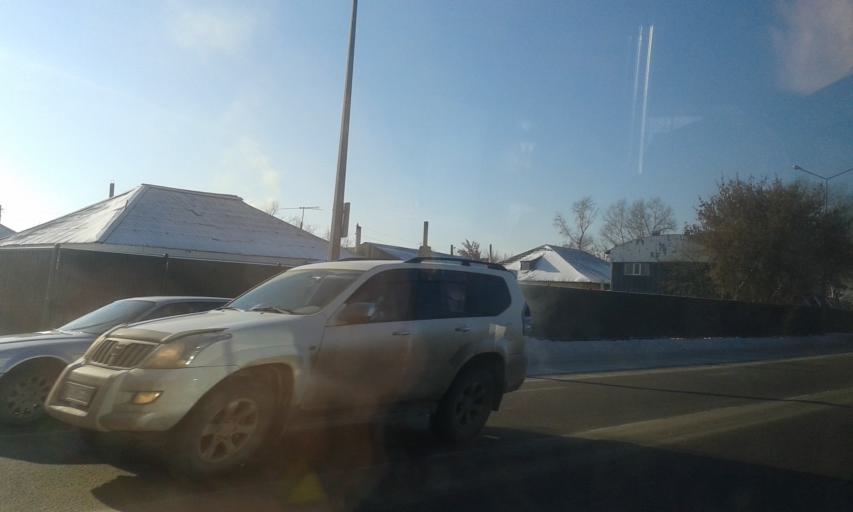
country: KZ
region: Astana Qalasy
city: Astana
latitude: 51.1569
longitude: 71.4506
